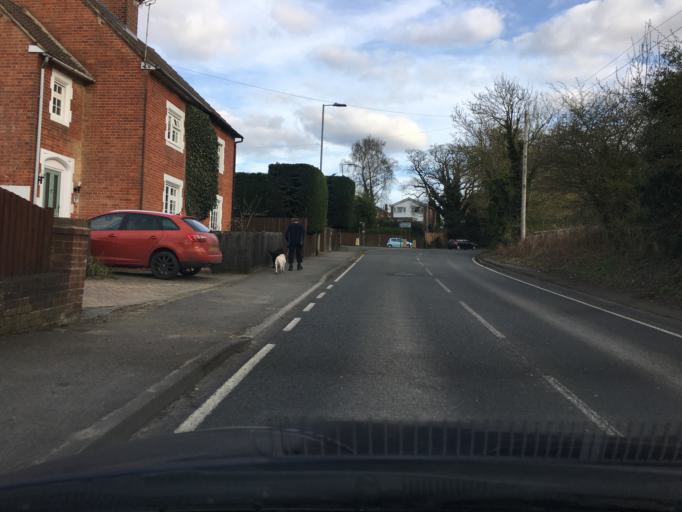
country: GB
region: England
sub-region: Hampshire
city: Yateley
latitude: 51.3531
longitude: -0.8153
